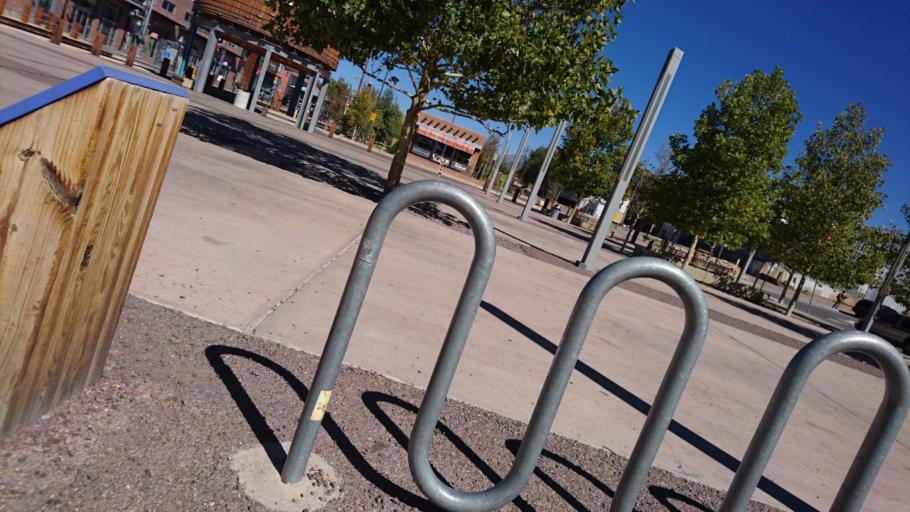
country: US
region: New Mexico
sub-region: Santa Fe County
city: Santa Fe
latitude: 35.6827
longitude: -105.9488
